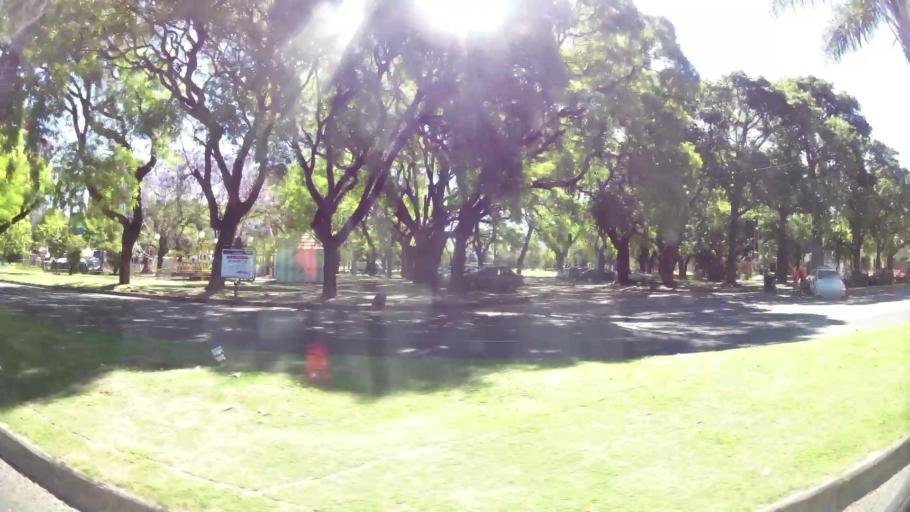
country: AR
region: Santa Fe
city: Santa Fe de la Vera Cruz
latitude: -31.6236
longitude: -60.6788
